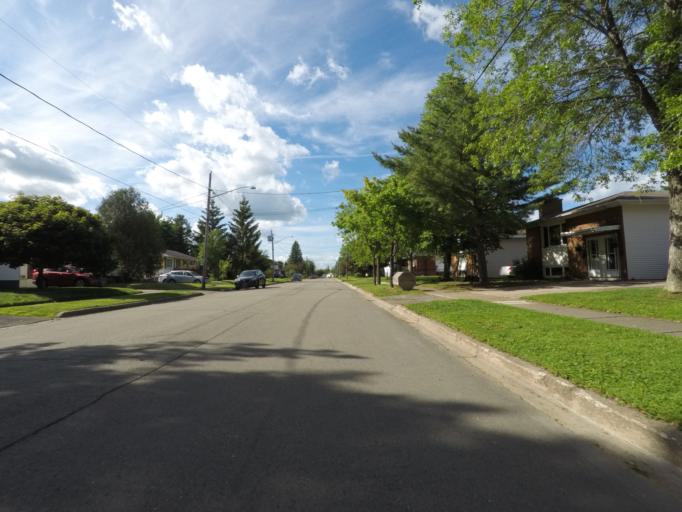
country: CA
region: New Brunswick
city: Moncton
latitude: 46.1010
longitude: -64.8256
